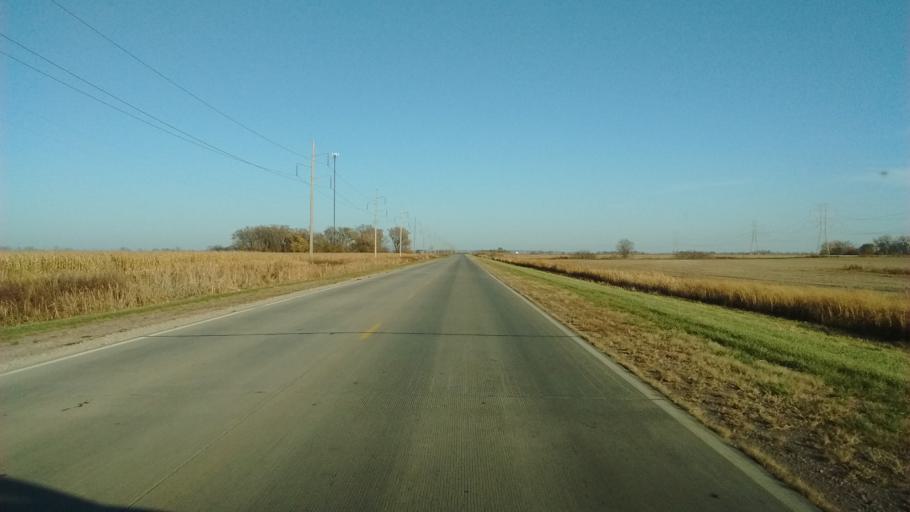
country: US
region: Iowa
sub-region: Woodbury County
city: Sergeant Bluff
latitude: 42.3302
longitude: -96.3433
